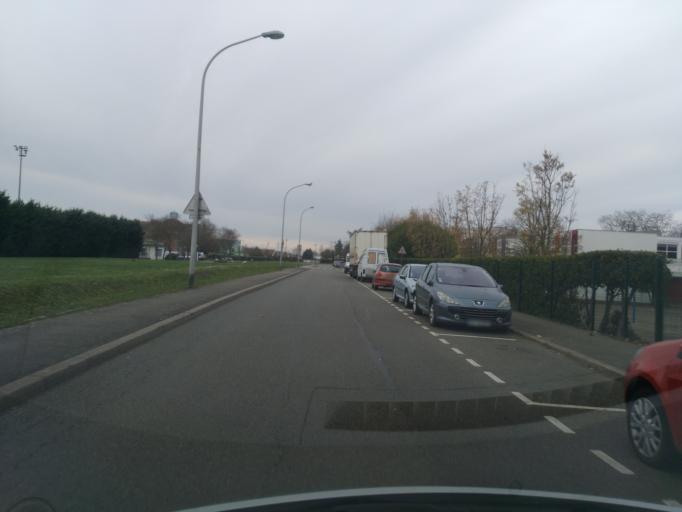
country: FR
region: Ile-de-France
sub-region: Departement des Yvelines
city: Plaisir
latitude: 48.8201
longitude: 1.9544
